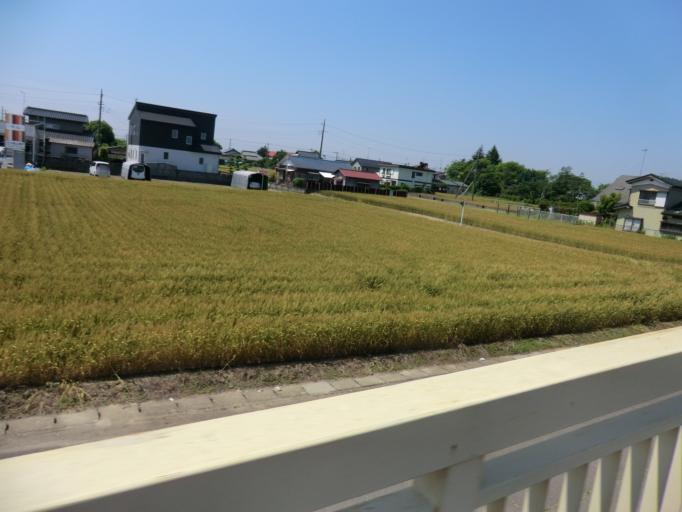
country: JP
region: Ibaraki
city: Ishige
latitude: 36.1102
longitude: 139.9761
